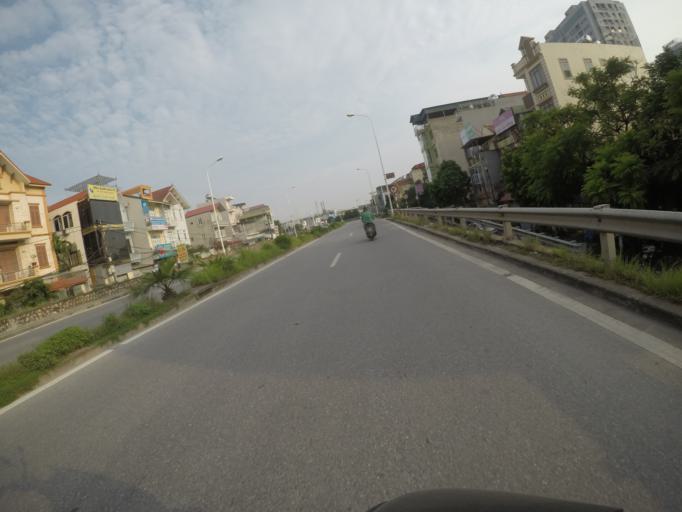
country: VN
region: Ha Noi
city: Tay Ho
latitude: 21.0880
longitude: 105.8149
